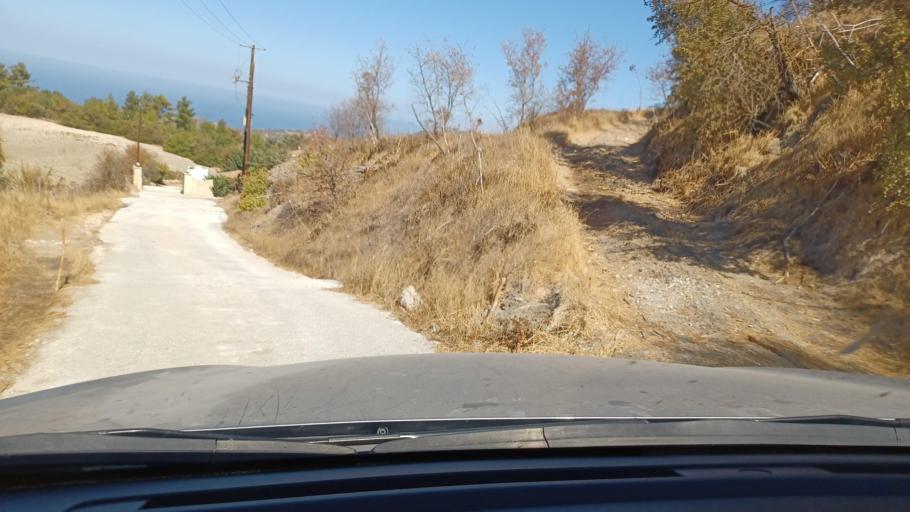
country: CY
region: Pafos
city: Polis
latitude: 35.0030
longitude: 32.5113
